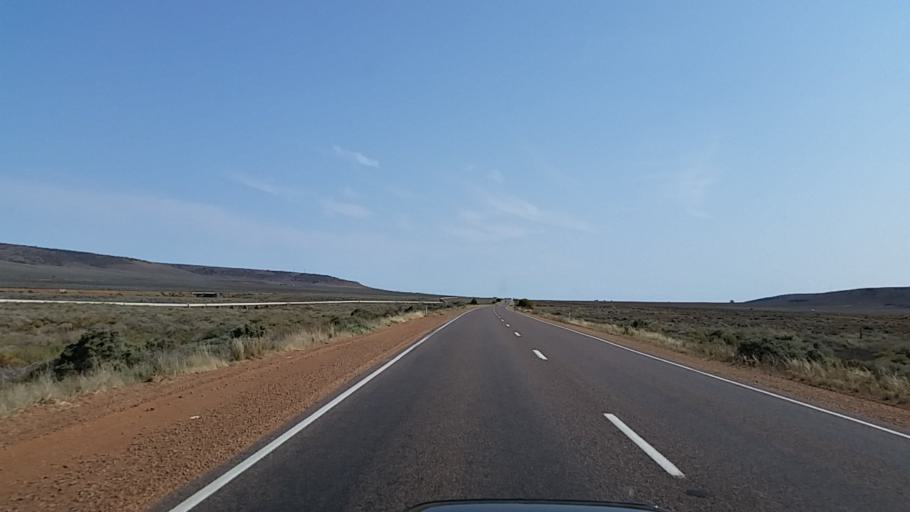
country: AU
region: South Australia
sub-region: Port Augusta
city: Port Augusta West
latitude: -32.5844
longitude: 137.6171
